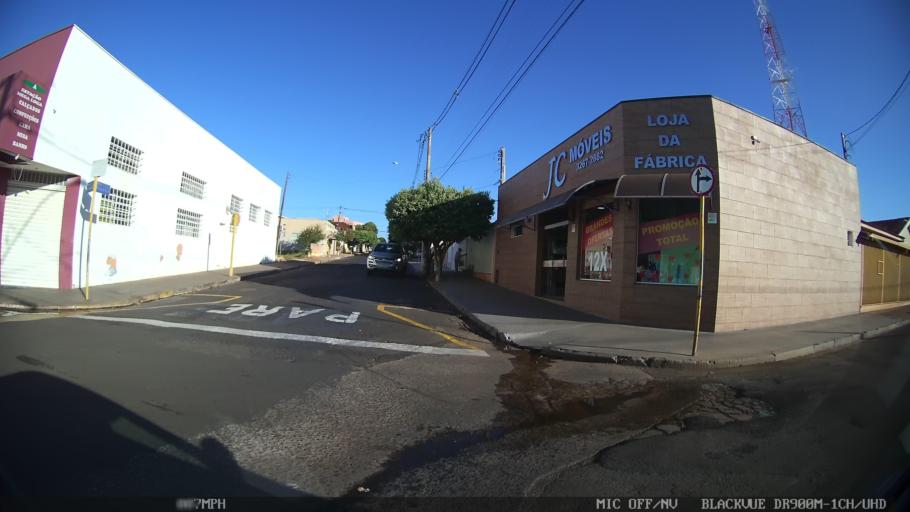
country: BR
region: Sao Paulo
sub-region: Guapiacu
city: Guapiacu
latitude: -20.7942
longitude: -49.2229
